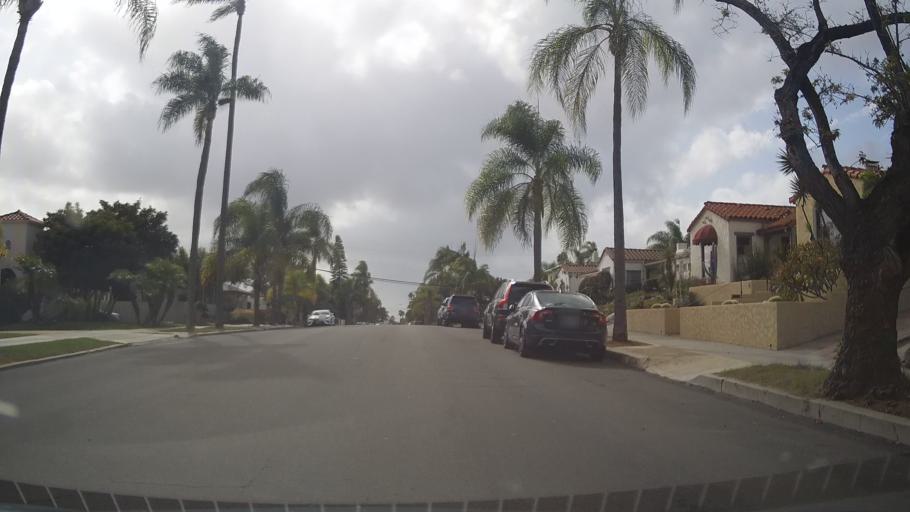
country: US
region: California
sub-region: San Diego County
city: San Diego
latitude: 32.7328
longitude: -117.1243
